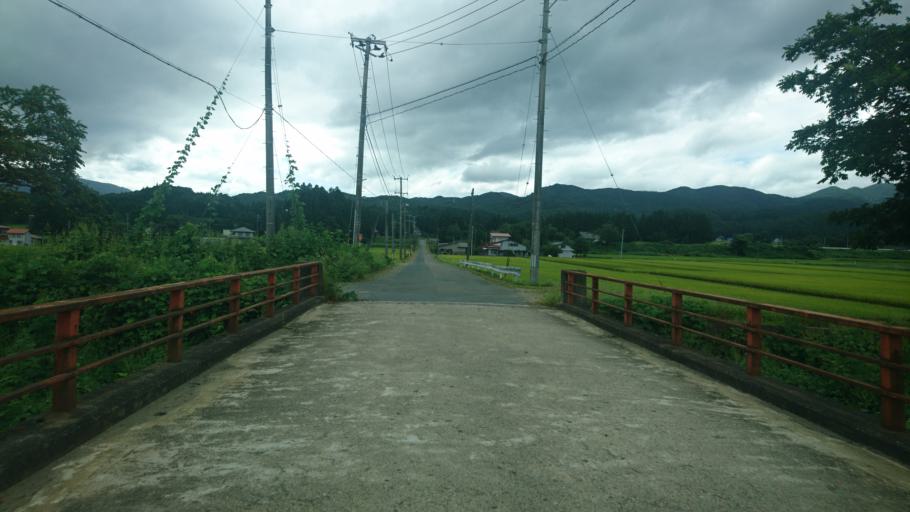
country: JP
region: Iwate
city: Kitakami
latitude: 39.3214
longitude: 140.9815
